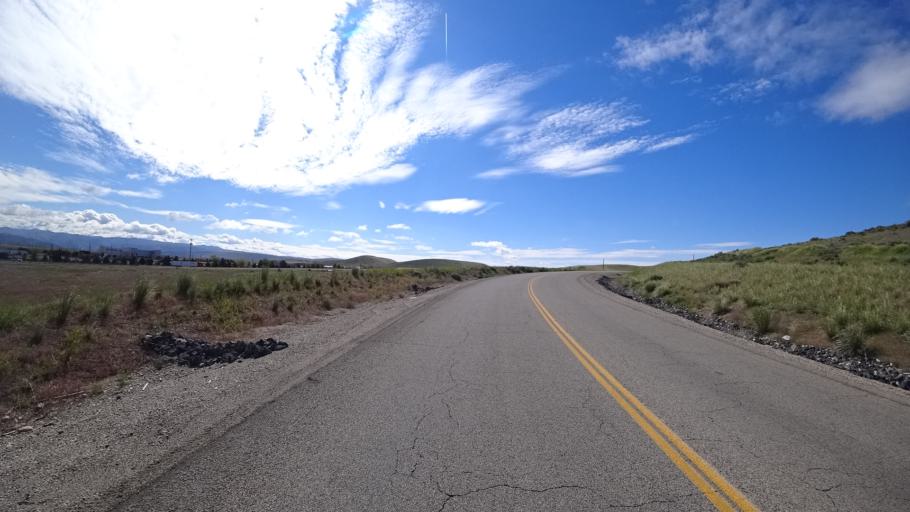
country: US
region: Idaho
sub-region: Ada County
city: Boise
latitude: 43.5111
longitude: -116.1487
